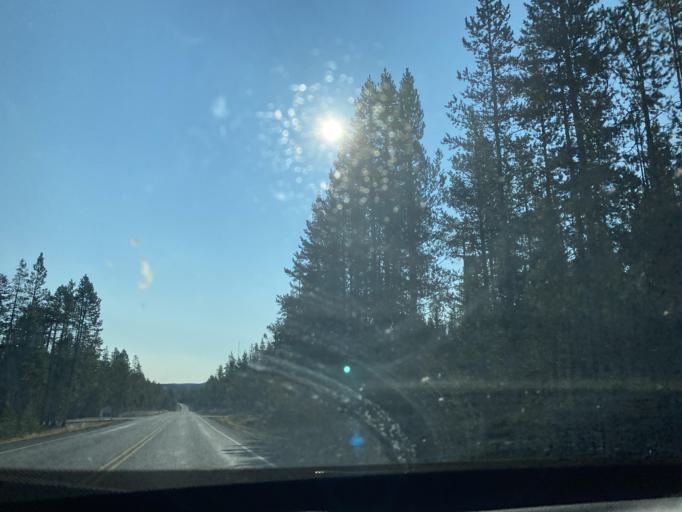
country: US
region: Oregon
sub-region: Deschutes County
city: Three Rivers
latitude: 43.7041
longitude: -121.2570
